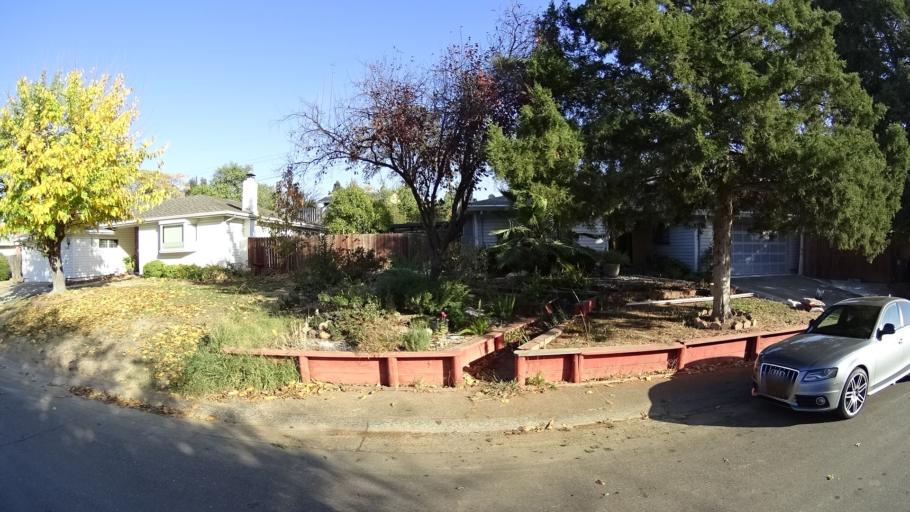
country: US
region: California
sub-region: Sacramento County
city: Fair Oaks
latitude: 38.6713
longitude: -121.2880
